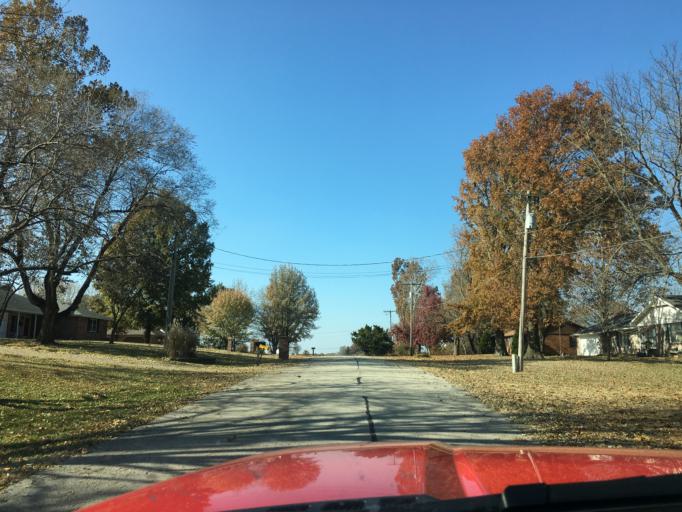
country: US
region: Missouri
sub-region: Cole County
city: Wardsville
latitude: 38.4855
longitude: -92.1738
